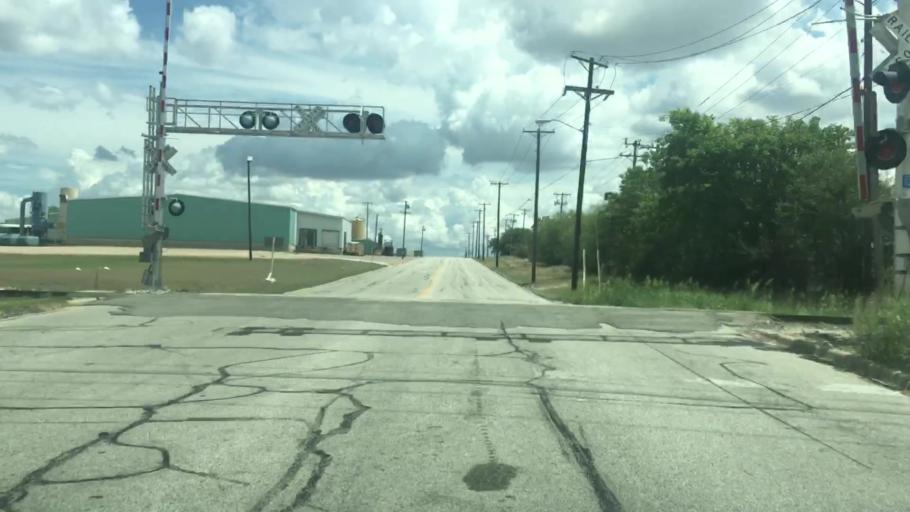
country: US
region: Texas
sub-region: Bell County
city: Temple
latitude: 31.1286
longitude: -97.3493
